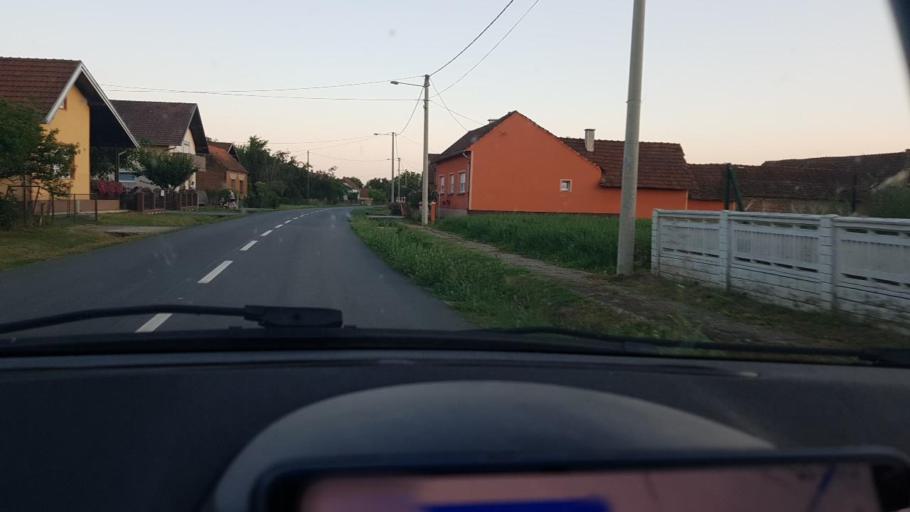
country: HR
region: Bjelovarsko-Bilogorska
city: Zdralovi
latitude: 45.8574
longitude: 16.9820
